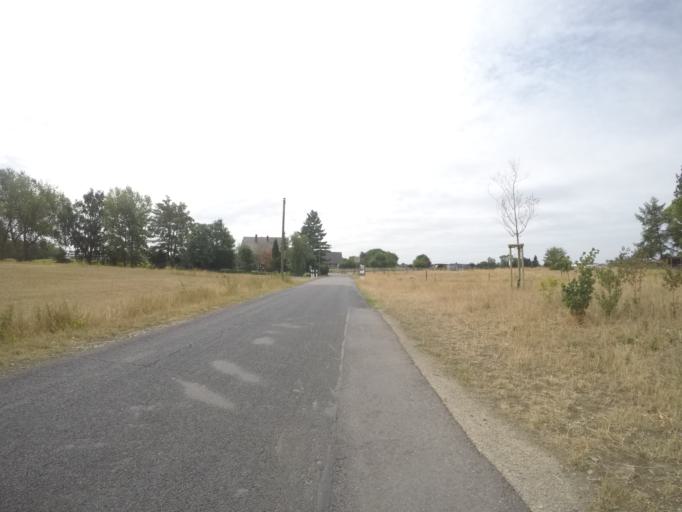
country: DE
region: North Rhine-Westphalia
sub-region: Regierungsbezirk Dusseldorf
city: Bocholt
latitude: 51.8492
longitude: 6.5909
